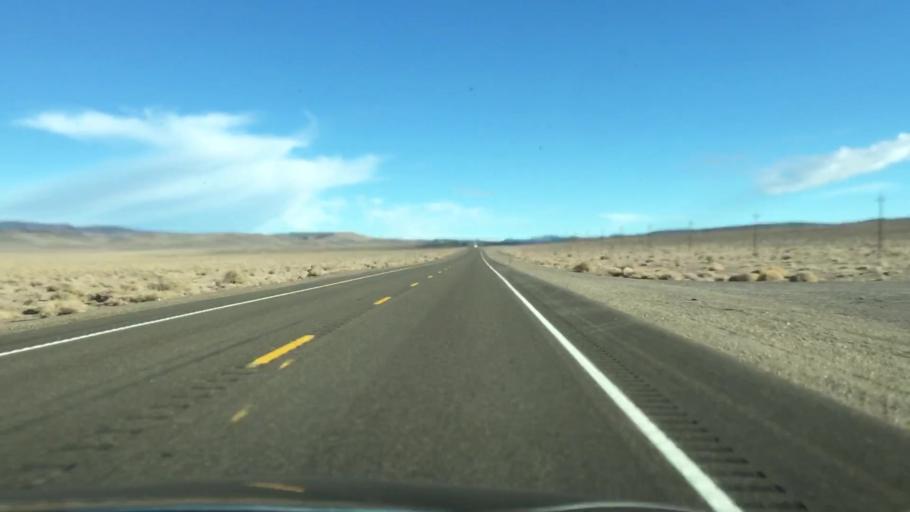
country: US
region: Nevada
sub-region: Mineral County
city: Hawthorne
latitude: 38.2533
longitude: -118.0792
